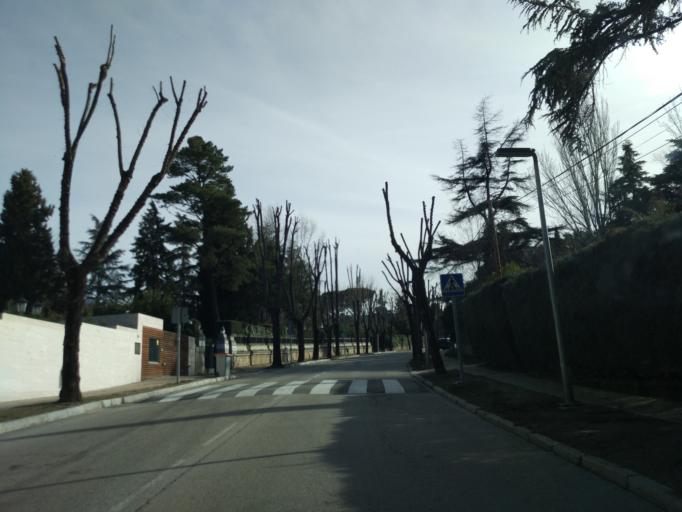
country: ES
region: Madrid
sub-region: Provincia de Madrid
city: Tetuan de las Victorias
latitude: 40.4681
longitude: -3.7312
